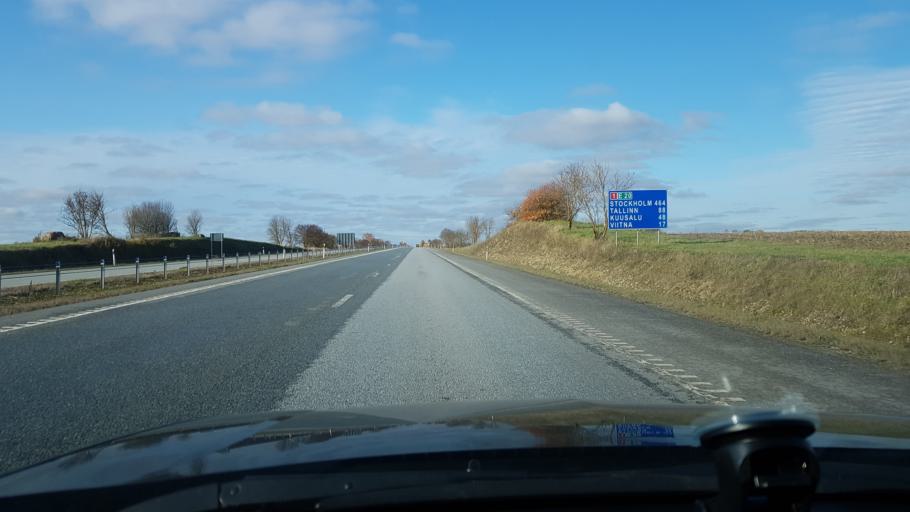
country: EE
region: Laeaene-Virumaa
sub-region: Haljala vald
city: Haljala
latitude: 59.4252
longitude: 26.2596
